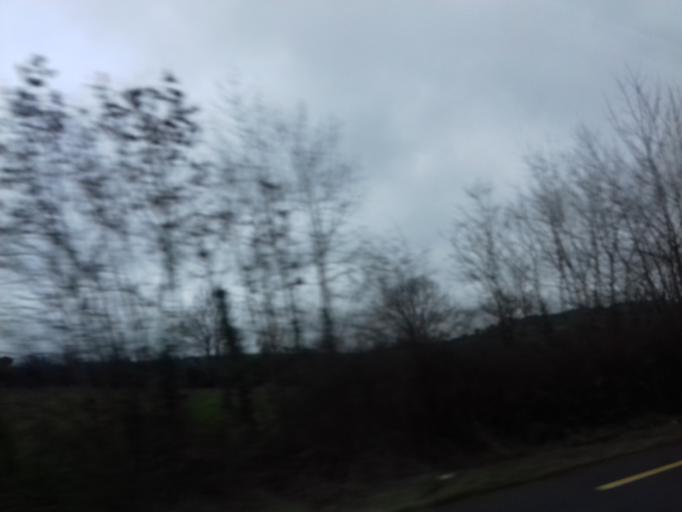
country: IE
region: Ulster
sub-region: County Monaghan
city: Castleblayney
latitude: 54.0897
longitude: -6.6947
